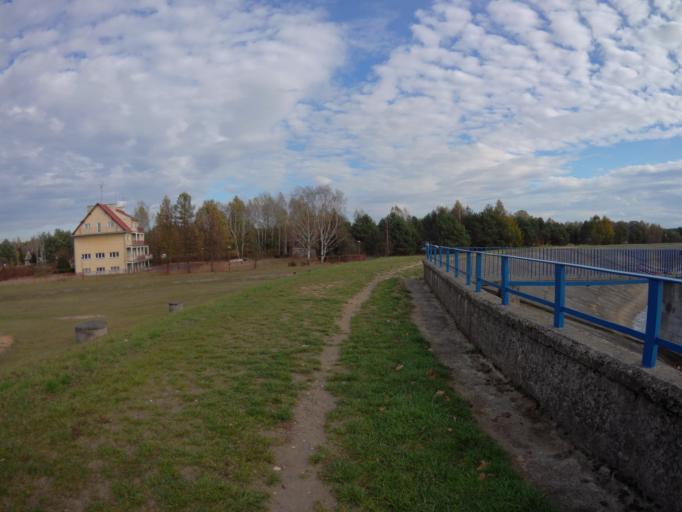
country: PL
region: Subcarpathian Voivodeship
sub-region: Powiat kolbuszowski
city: Lipnica
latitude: 50.3417
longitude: 21.9339
